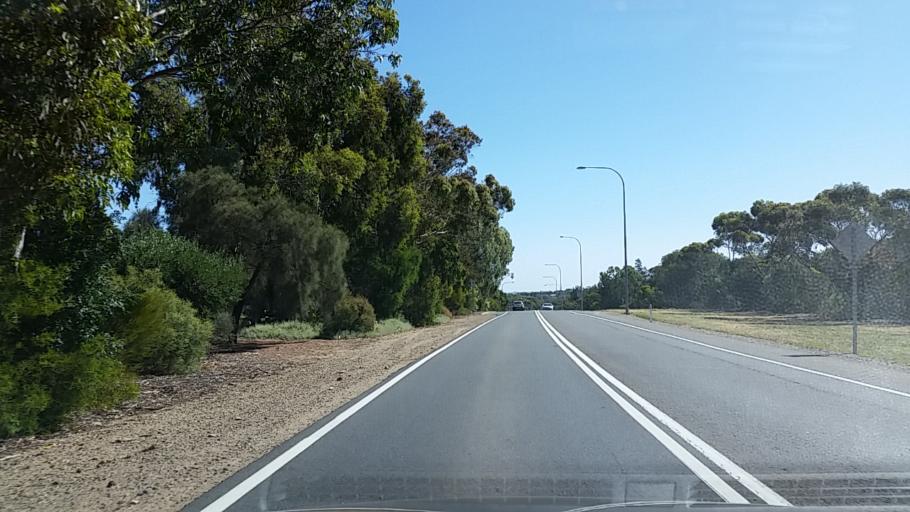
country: AU
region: South Australia
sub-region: Tea Tree Gully
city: Hope Valley
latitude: -34.8025
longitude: 138.7046
